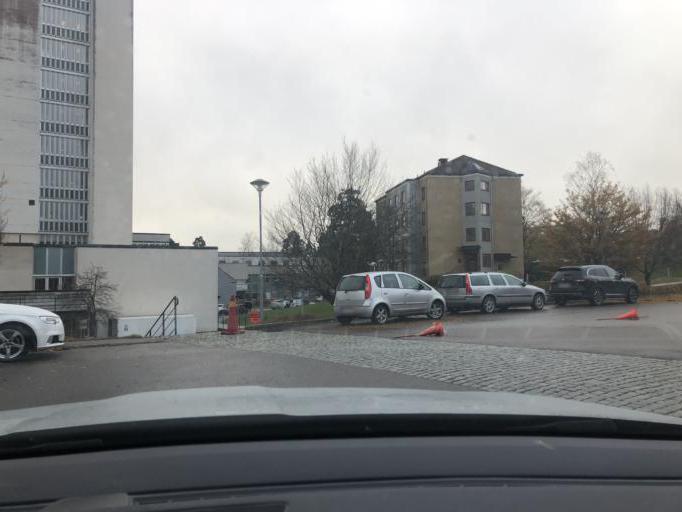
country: SE
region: Soedermanland
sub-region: Nykopings Kommun
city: Nykoping
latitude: 58.7610
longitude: 16.9949
